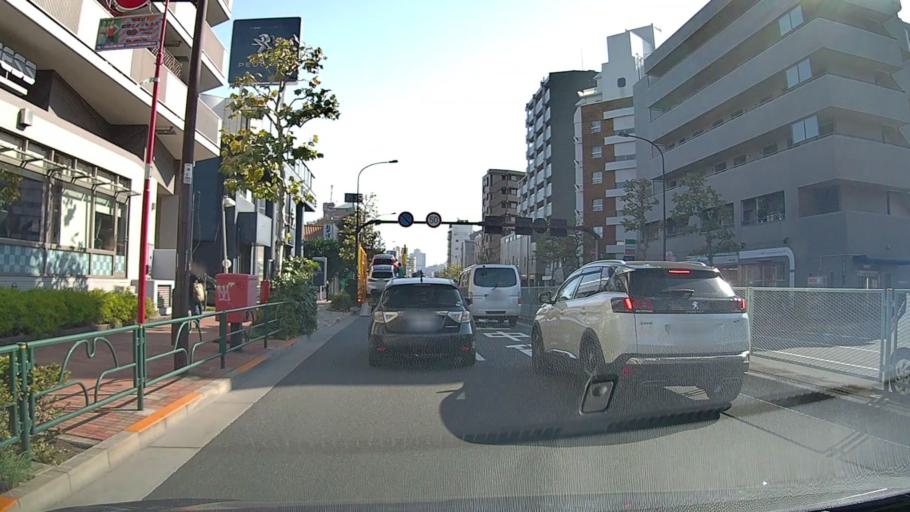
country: JP
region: Tokyo
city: Tokyo
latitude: 35.7326
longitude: 139.6706
